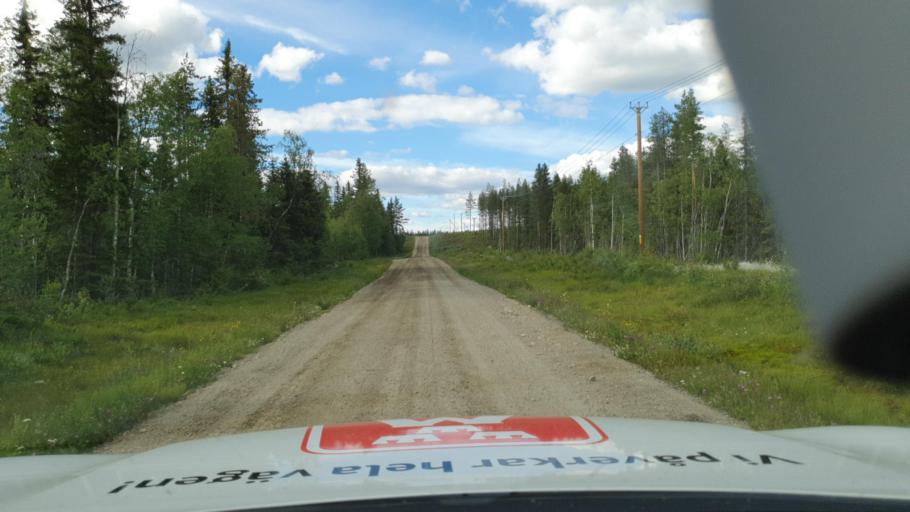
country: SE
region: Vaesterbotten
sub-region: Lycksele Kommun
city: Lycksele
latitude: 64.2993
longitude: 18.2887
